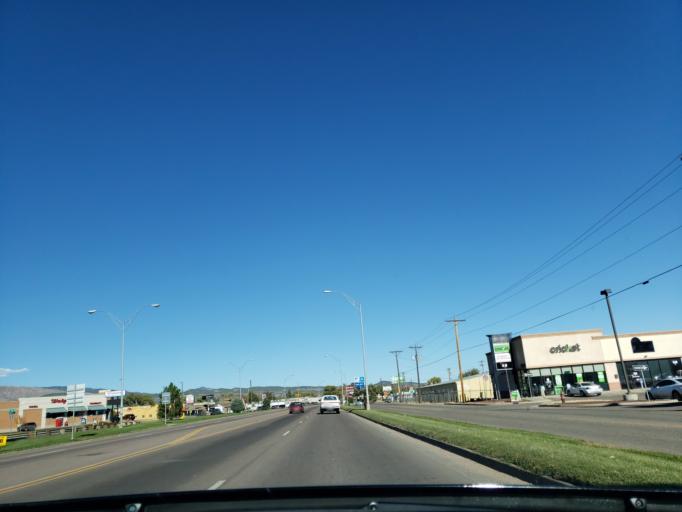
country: US
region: Colorado
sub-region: Fremont County
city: Canon City
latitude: 38.4462
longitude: -105.2263
